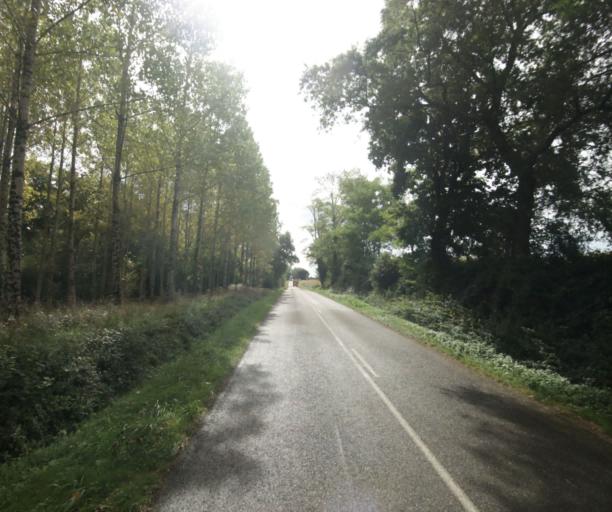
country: FR
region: Midi-Pyrenees
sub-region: Departement du Gers
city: Cazaubon
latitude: 43.8823
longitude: -0.0984
